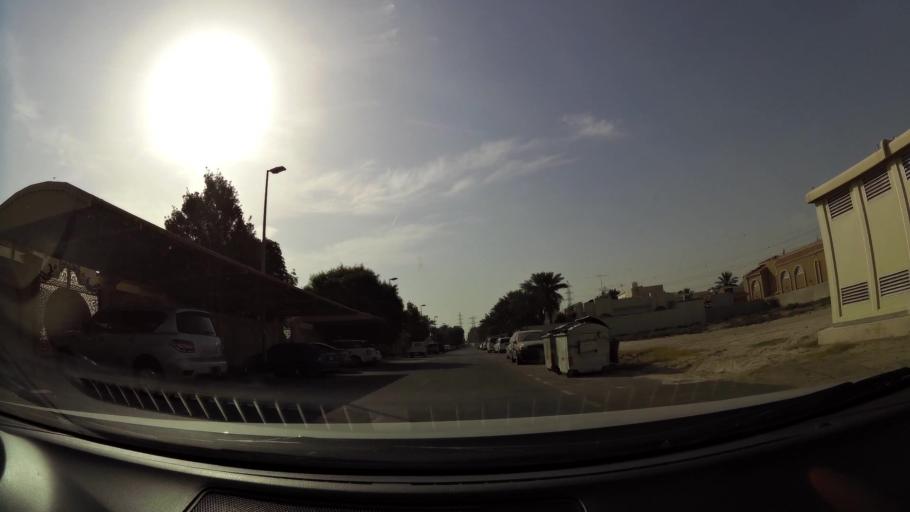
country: AE
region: Ash Shariqah
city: Sharjah
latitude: 25.2156
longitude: 55.3854
